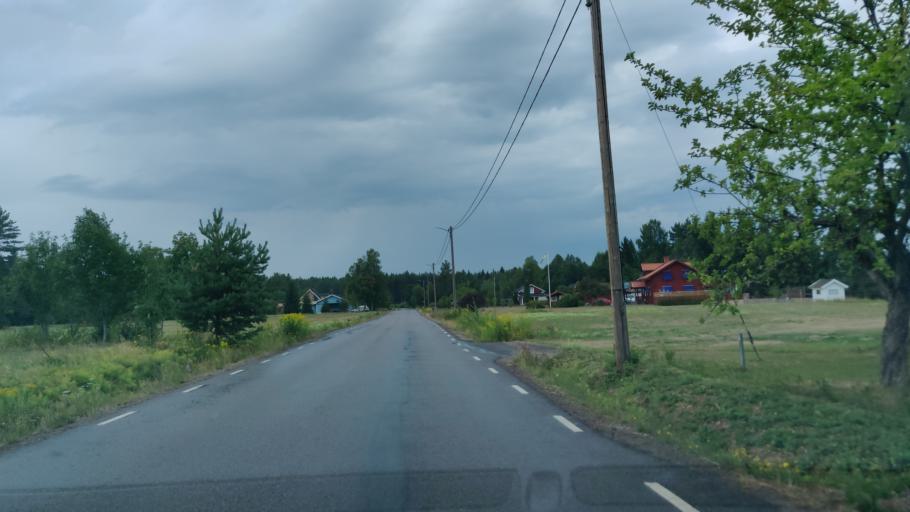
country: SE
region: Vaermland
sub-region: Munkfors Kommun
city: Munkfors
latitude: 59.8636
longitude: 13.5467
